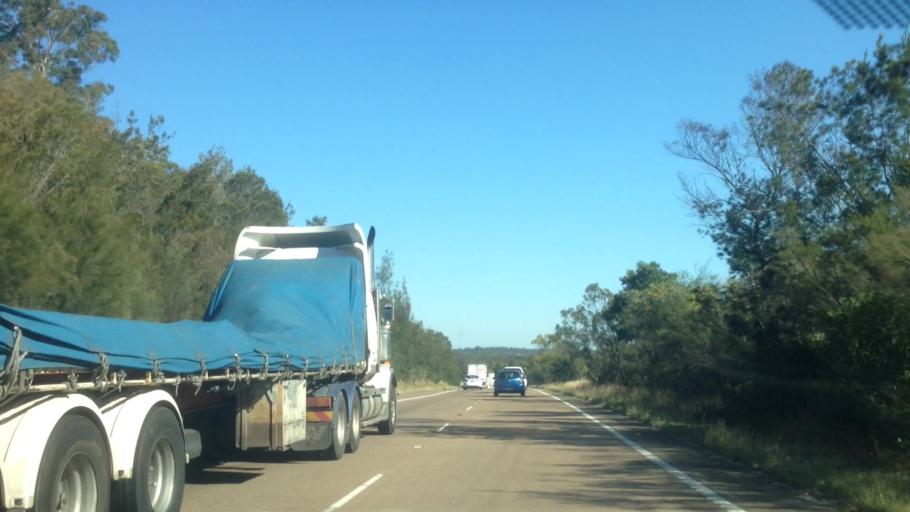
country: AU
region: New South Wales
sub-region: Lake Macquarie Shire
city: Dora Creek
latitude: -33.1511
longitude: 151.4729
